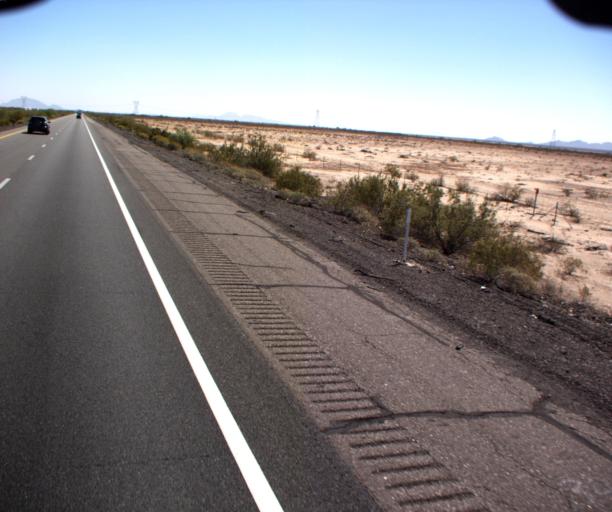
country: US
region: Arizona
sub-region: La Paz County
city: Salome
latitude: 33.5786
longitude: -113.4185
